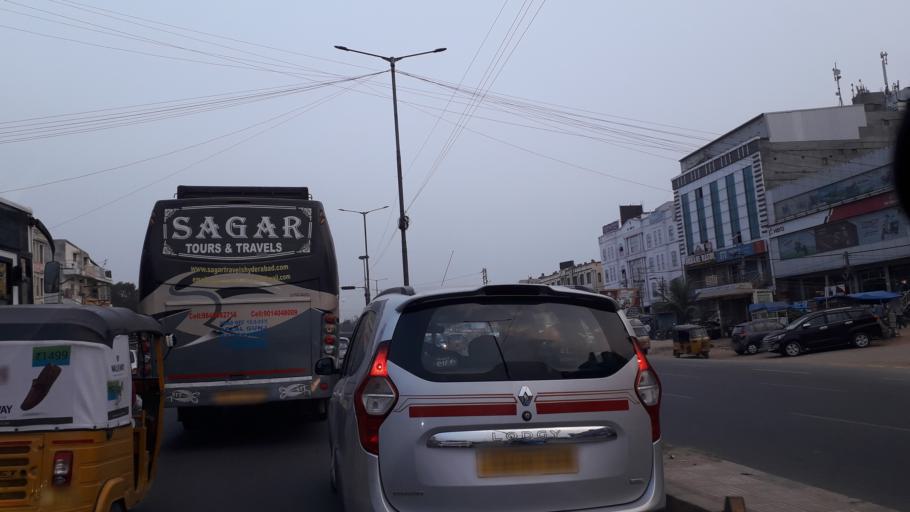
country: IN
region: Telangana
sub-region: Medak
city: Serilingampalle
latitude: 17.5096
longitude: 78.2994
